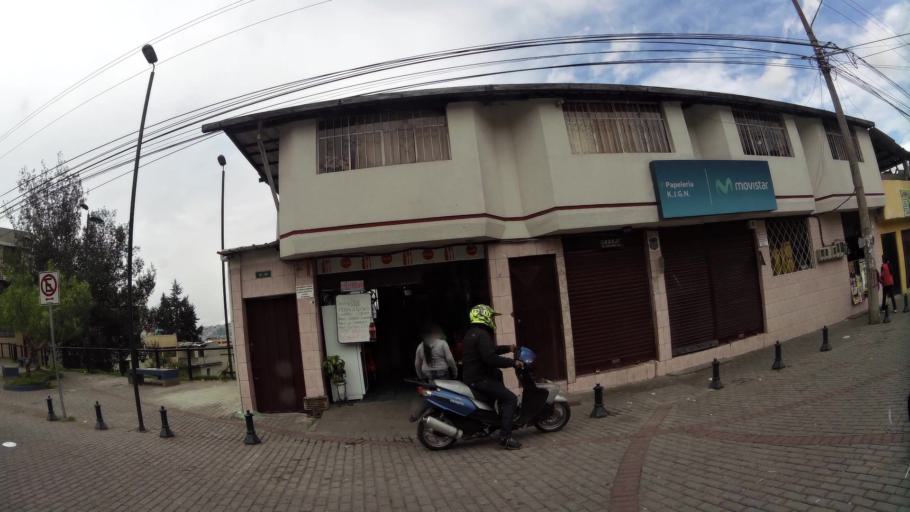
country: EC
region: Pichincha
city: Quito
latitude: -0.2126
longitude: -78.5167
